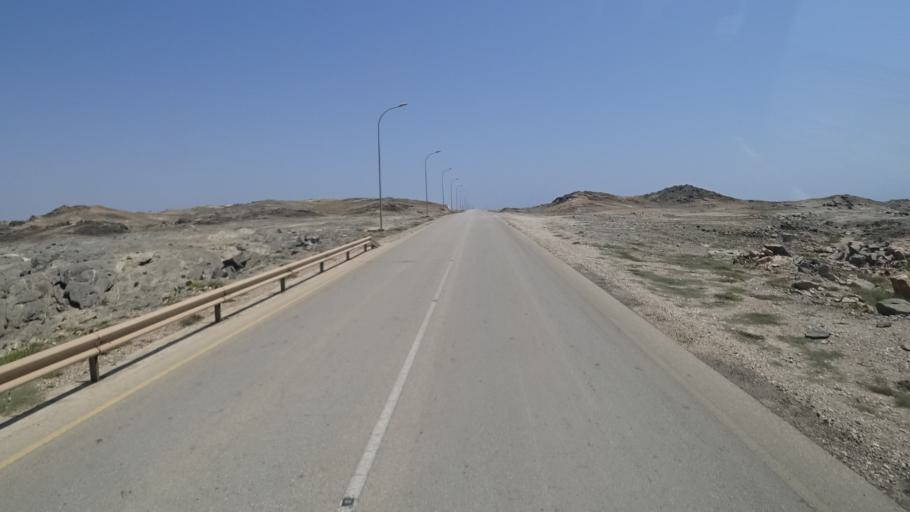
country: OM
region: Zufar
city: Salalah
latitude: 16.9705
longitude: 54.7245
